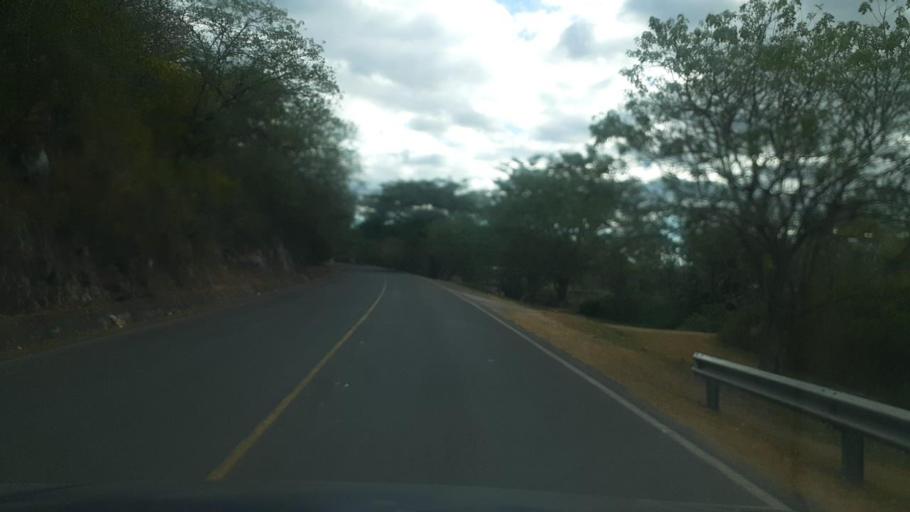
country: NI
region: Madriz
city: Somoto
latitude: 13.4968
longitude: -86.5739
